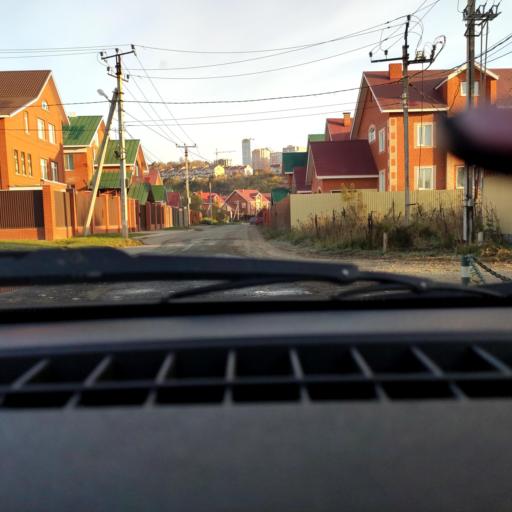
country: RU
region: Bashkortostan
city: Ufa
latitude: 54.6910
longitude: 55.9776
